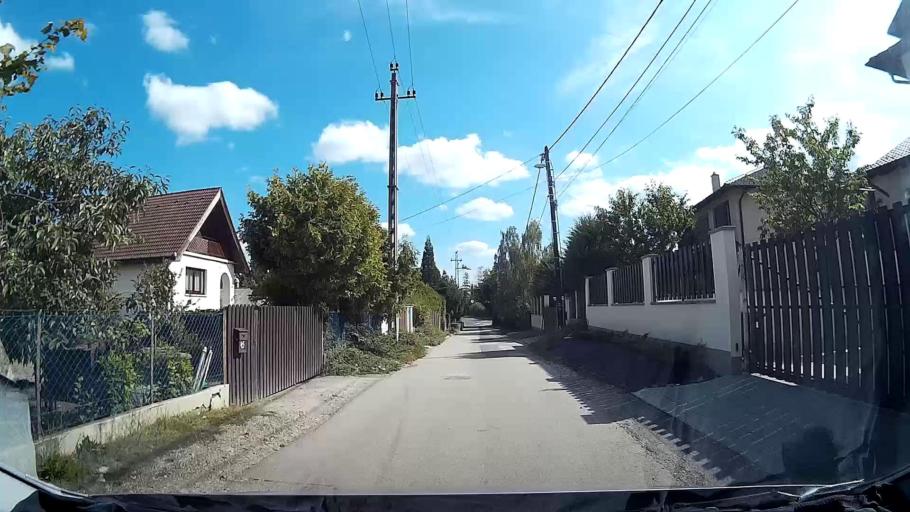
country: HU
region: Pest
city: Szentendre
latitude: 47.6804
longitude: 19.0711
